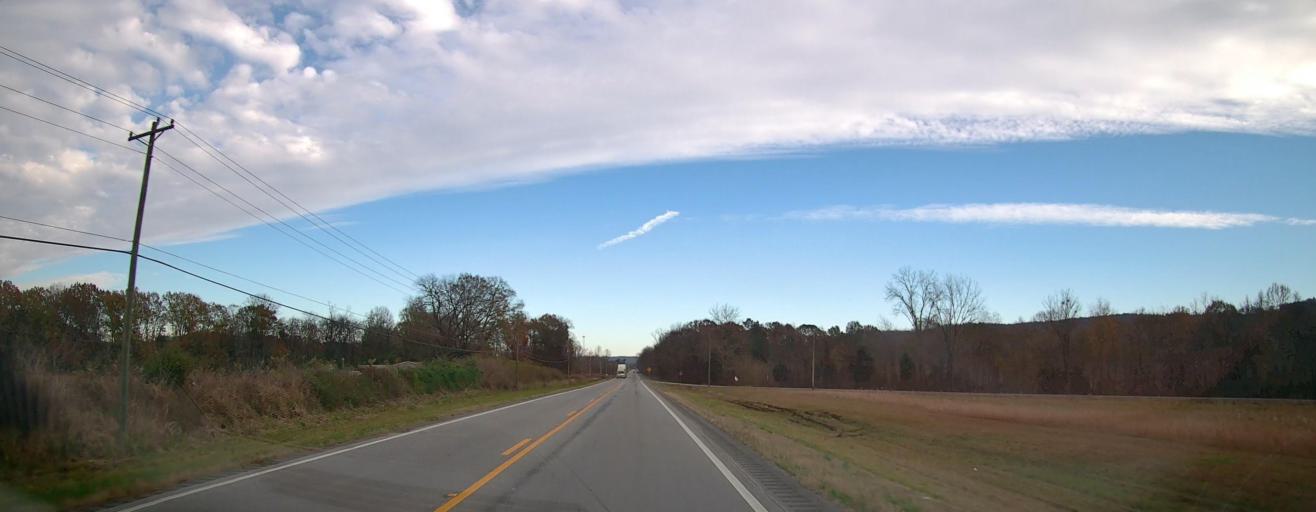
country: US
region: Alabama
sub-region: Morgan County
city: Falkville
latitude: 34.4246
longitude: -86.7199
